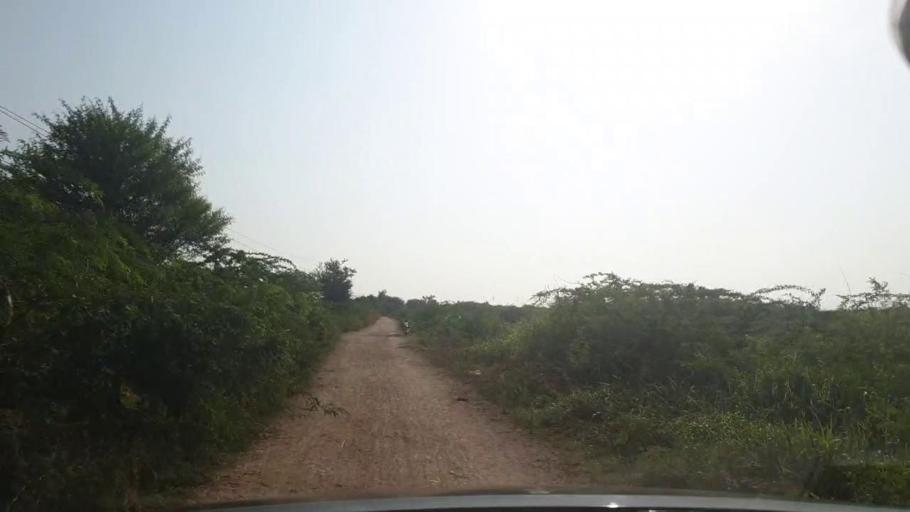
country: PK
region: Sindh
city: Tando Bago
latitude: 24.6509
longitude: 69.1717
